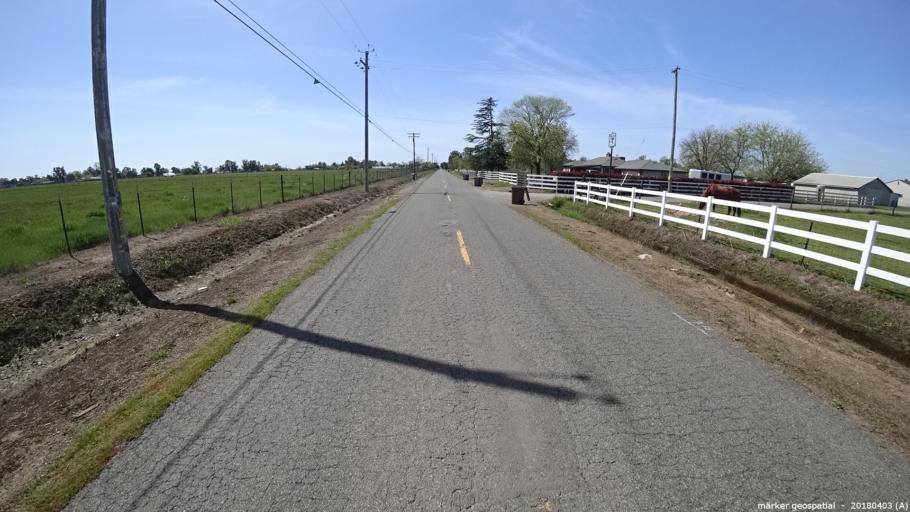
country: US
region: California
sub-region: Sacramento County
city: Herald
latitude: 38.3431
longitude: -121.2338
